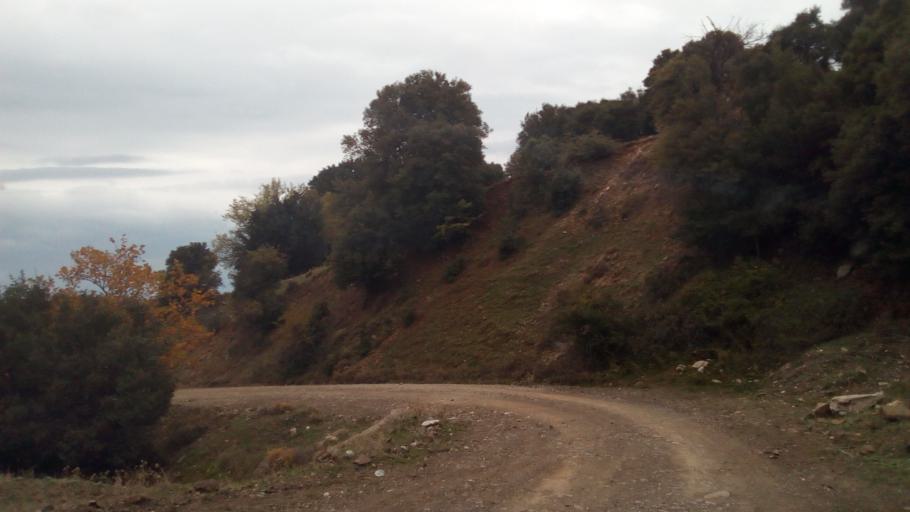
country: GR
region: West Greece
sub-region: Nomos Achaias
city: Selianitika
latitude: 38.4137
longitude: 22.0890
